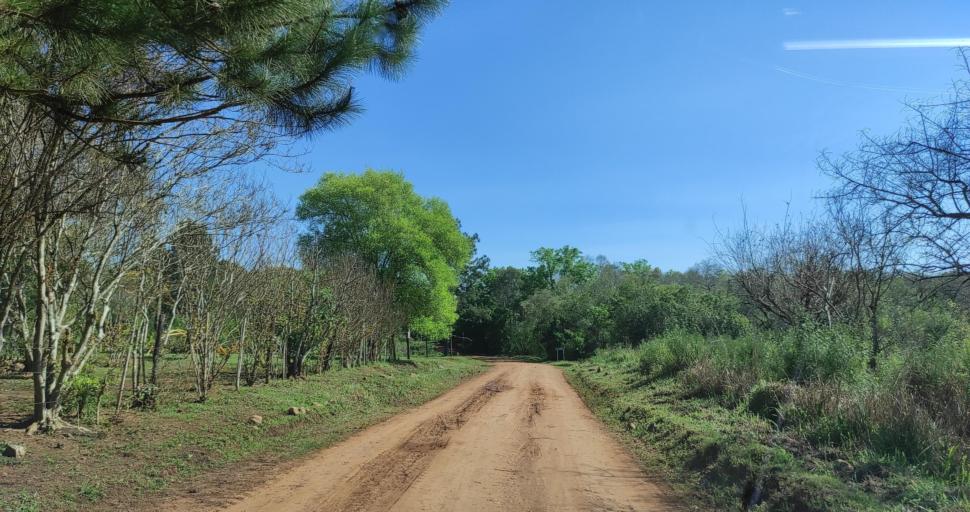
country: AR
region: Misiones
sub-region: Departamento de Candelaria
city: Loreto
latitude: -27.3127
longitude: -55.5370
